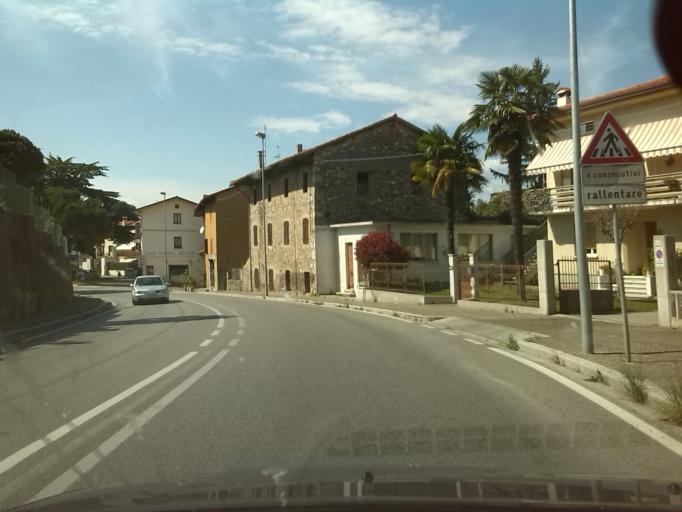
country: IT
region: Friuli Venezia Giulia
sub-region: Provincia di Udine
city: Fagagna
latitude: 46.1111
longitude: 13.0874
